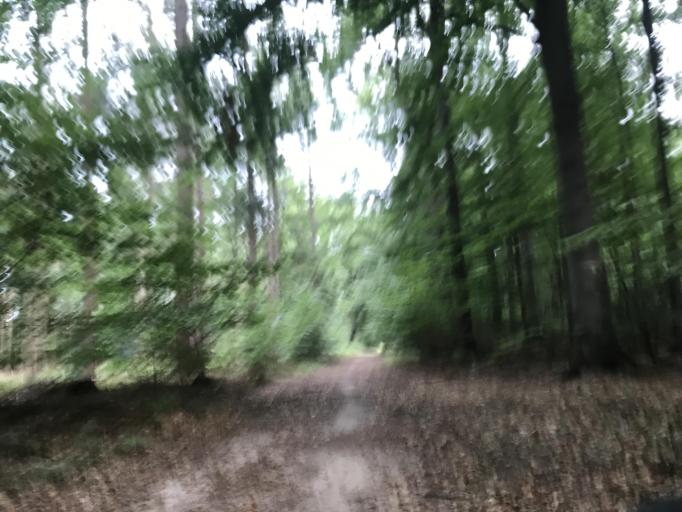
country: DE
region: Lower Saxony
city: Barendorf
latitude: 53.2169
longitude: 10.5368
